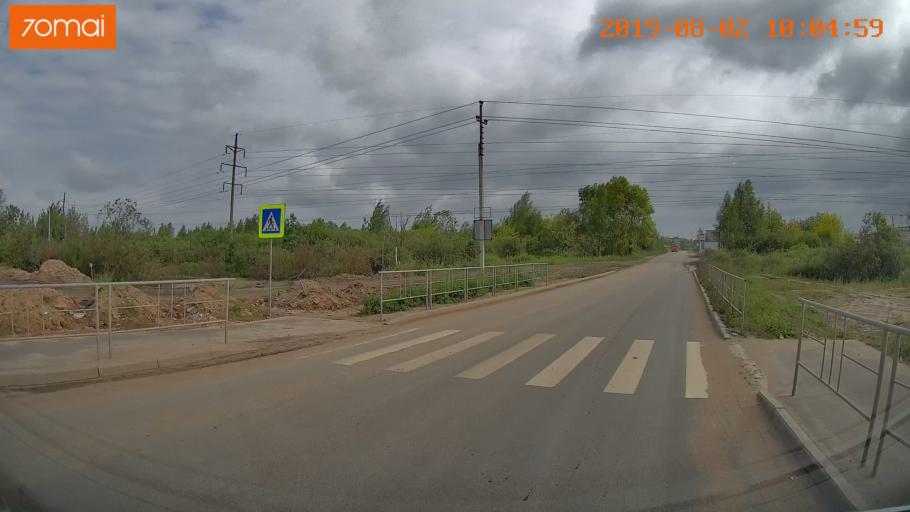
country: RU
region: Ivanovo
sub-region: Gorod Ivanovo
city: Ivanovo
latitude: 56.9764
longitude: 40.9217
